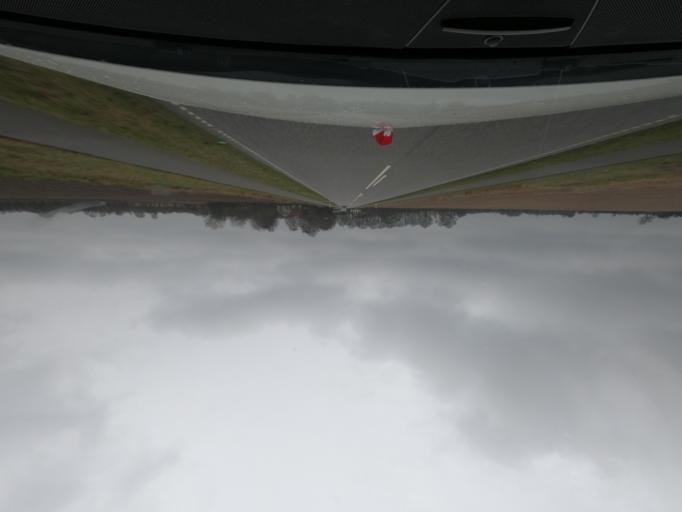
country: DK
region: South Denmark
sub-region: Haderslev Kommune
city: Starup
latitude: 55.2548
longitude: 9.6589
